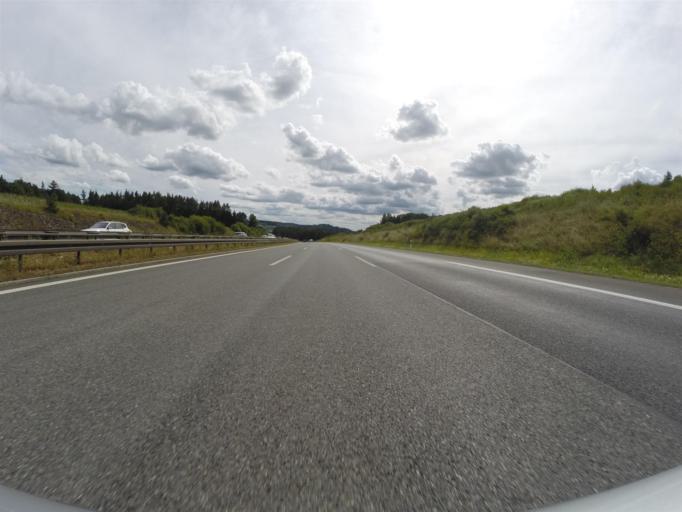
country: DE
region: Bavaria
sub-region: Upper Franconia
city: Haag
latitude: 49.8424
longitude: 11.5049
